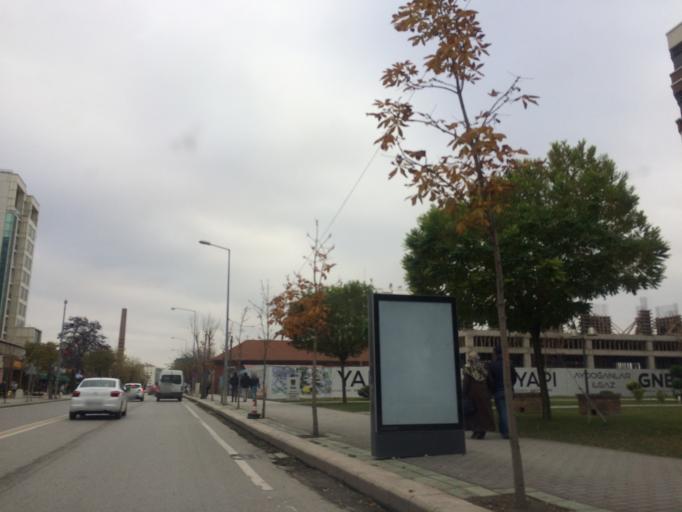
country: TR
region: Eskisehir
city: Eskisehir
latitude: 39.7832
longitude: 30.5055
